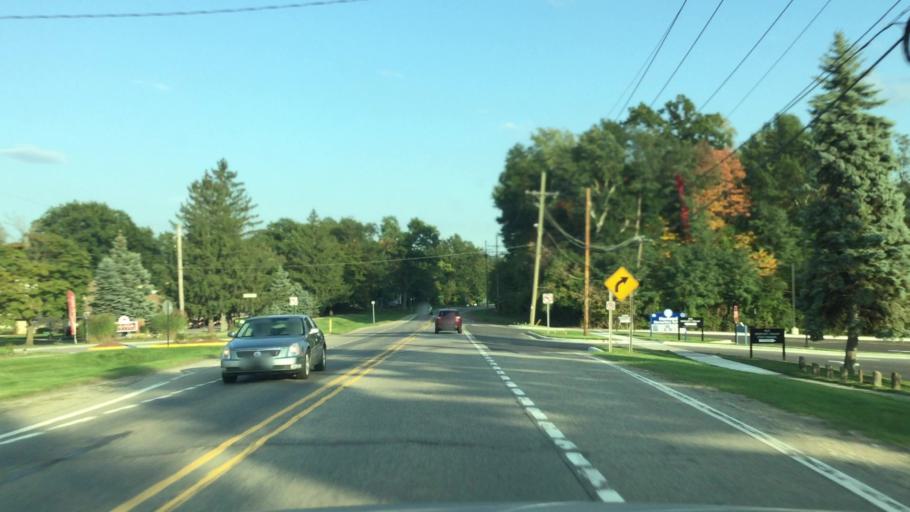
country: US
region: Michigan
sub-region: Oakland County
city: Keego Harbor
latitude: 42.6279
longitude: -83.3918
